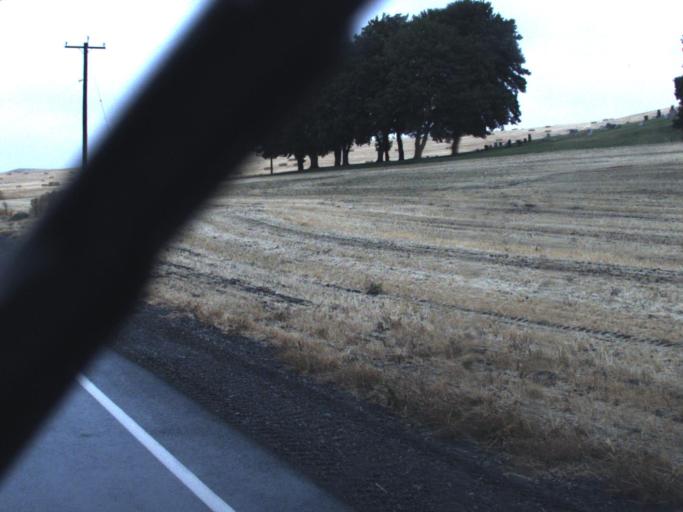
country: US
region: Washington
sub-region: Whitman County
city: Colfax
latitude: 47.0773
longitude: -117.5375
